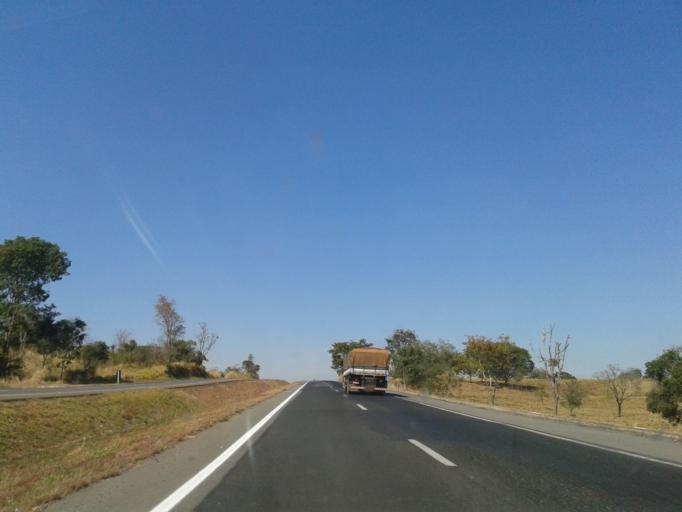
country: BR
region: Goias
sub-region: Piracanjuba
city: Piracanjuba
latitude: -17.3204
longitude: -49.2391
